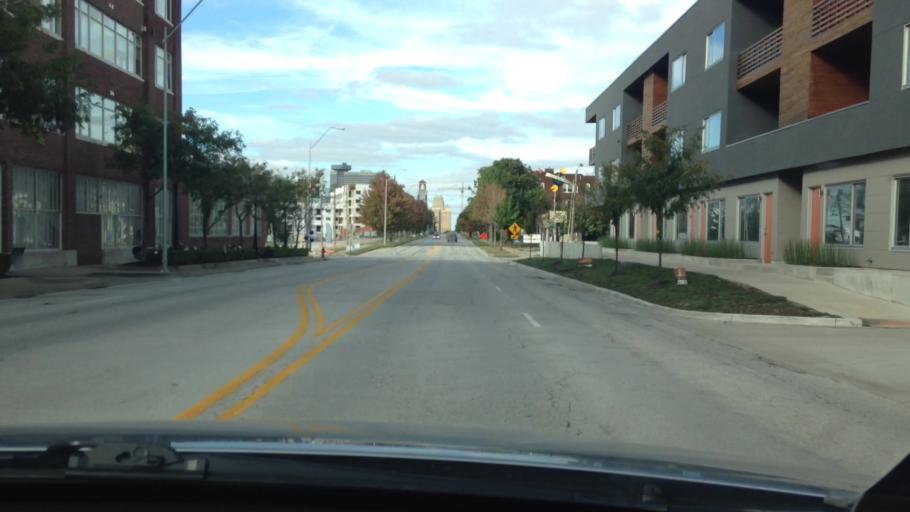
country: US
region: Missouri
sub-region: Jackson County
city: Kansas City
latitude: 39.0736
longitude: -94.5787
